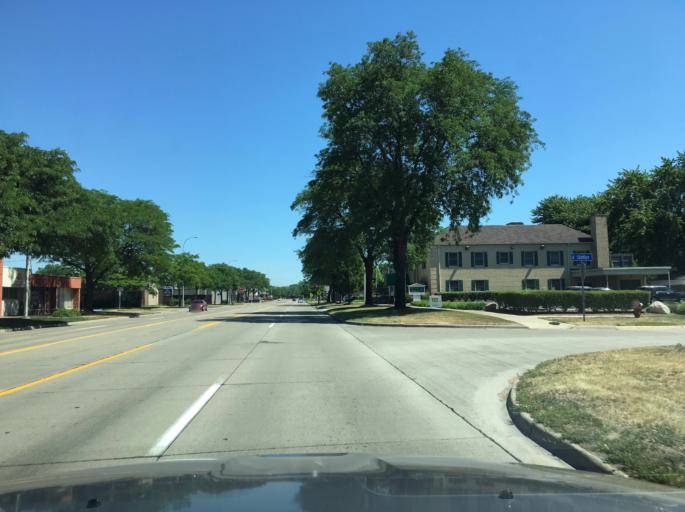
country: US
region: Michigan
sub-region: Macomb County
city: Saint Clair Shores
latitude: 42.4834
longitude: -82.9002
